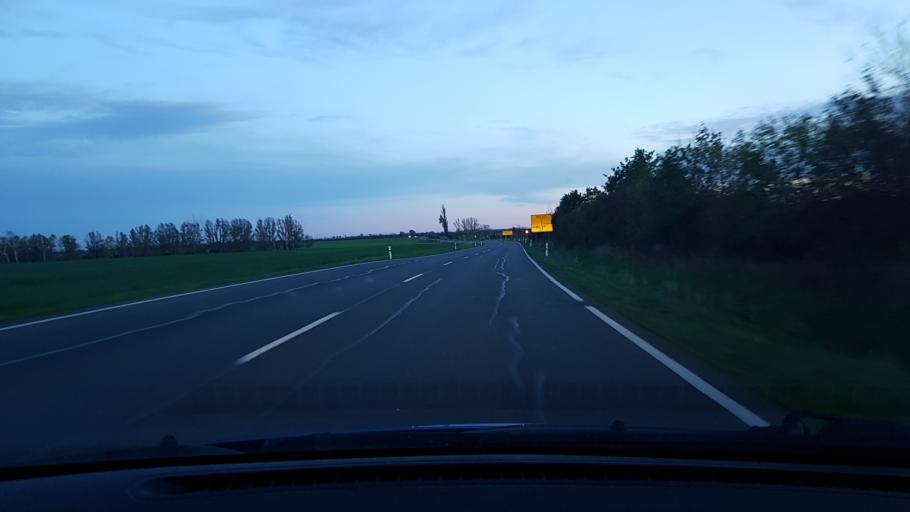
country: DE
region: Saxony-Anhalt
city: Zerbst
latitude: 52.0020
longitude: 12.0304
